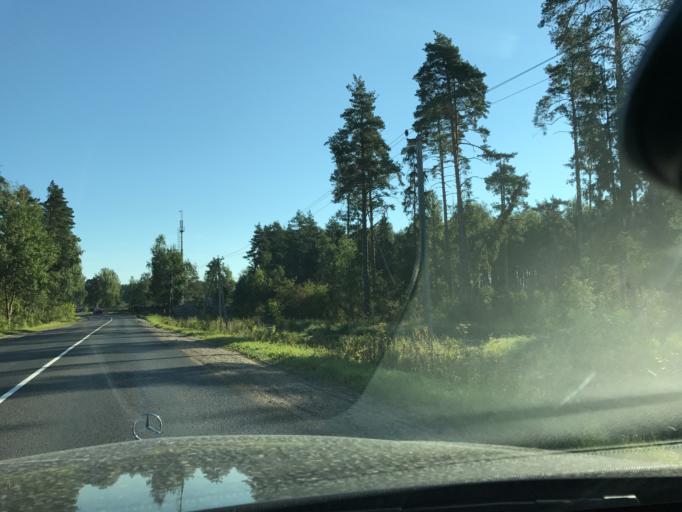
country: RU
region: Moskovskaya
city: Sverdlovskiy
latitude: 55.8653
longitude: 38.1516
